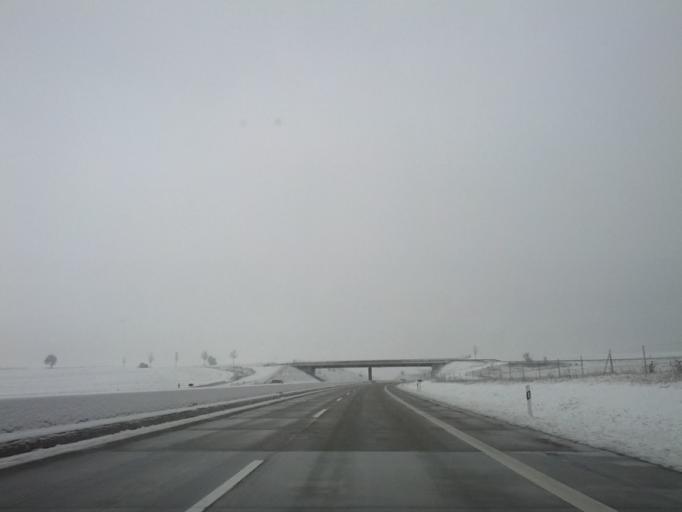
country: DE
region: Bavaria
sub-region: Regierungsbezirk Unterfranken
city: Rodelmaier
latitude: 50.3055
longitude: 10.2801
